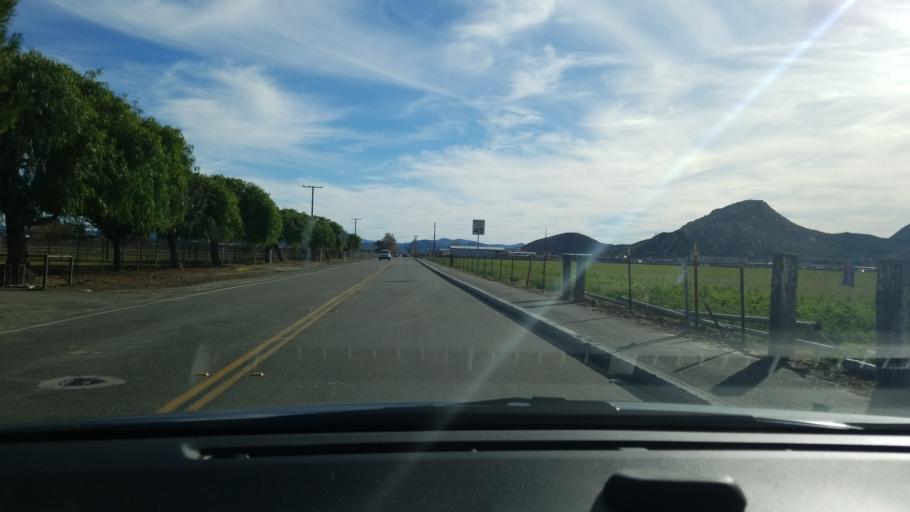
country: US
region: California
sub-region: Riverside County
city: Hemet
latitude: 33.7764
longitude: -117.0155
